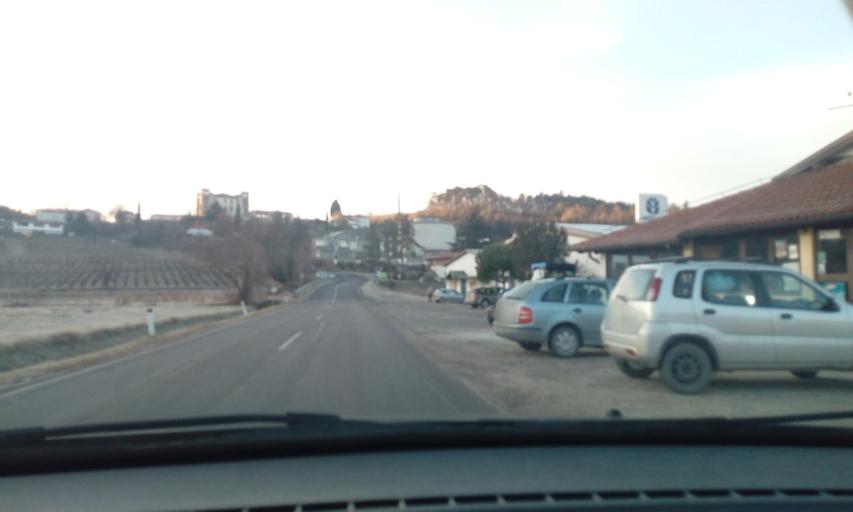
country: SI
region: Brda
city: Dobrovo
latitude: 46.0007
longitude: 13.5242
